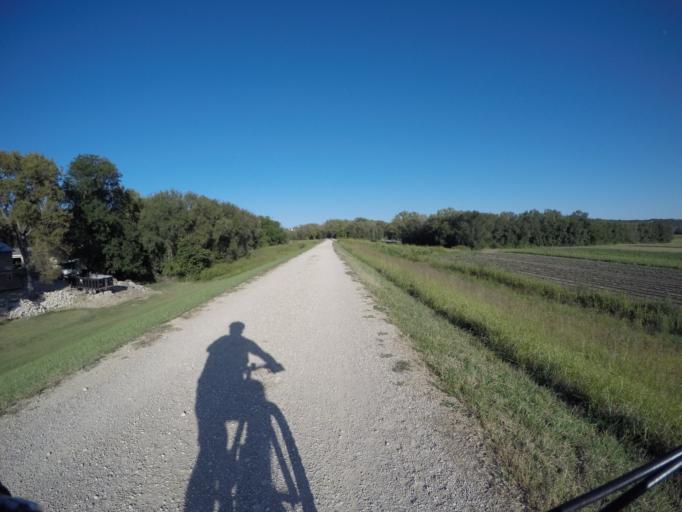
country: US
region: Kansas
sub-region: Riley County
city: Manhattan
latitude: 39.1708
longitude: -96.5655
